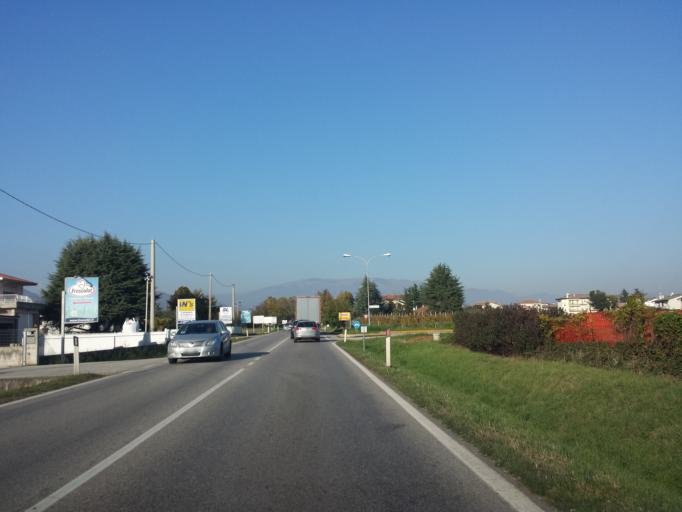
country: IT
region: Veneto
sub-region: Provincia di Treviso
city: Caerano di San Marco
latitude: 45.7829
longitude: 11.9937
